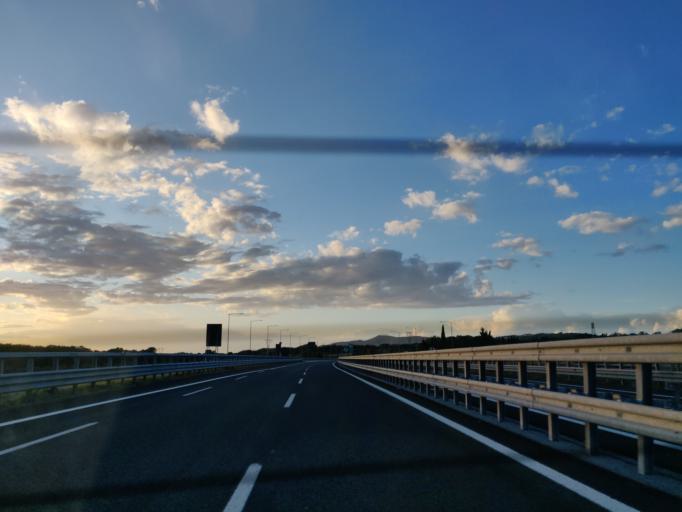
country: IT
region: Tuscany
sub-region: Provincia di Livorno
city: Rosignano Marittimo
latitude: 43.3759
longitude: 10.4999
